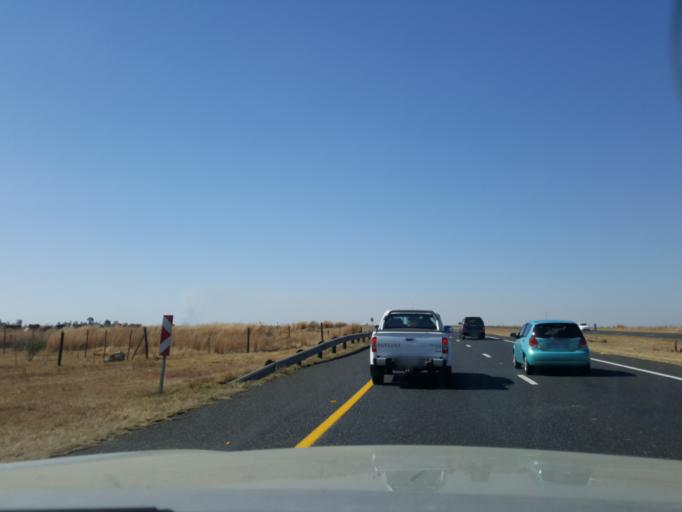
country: ZA
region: Mpumalanga
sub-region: Nkangala District Municipality
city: Delmas
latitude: -26.0666
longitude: 28.7886
